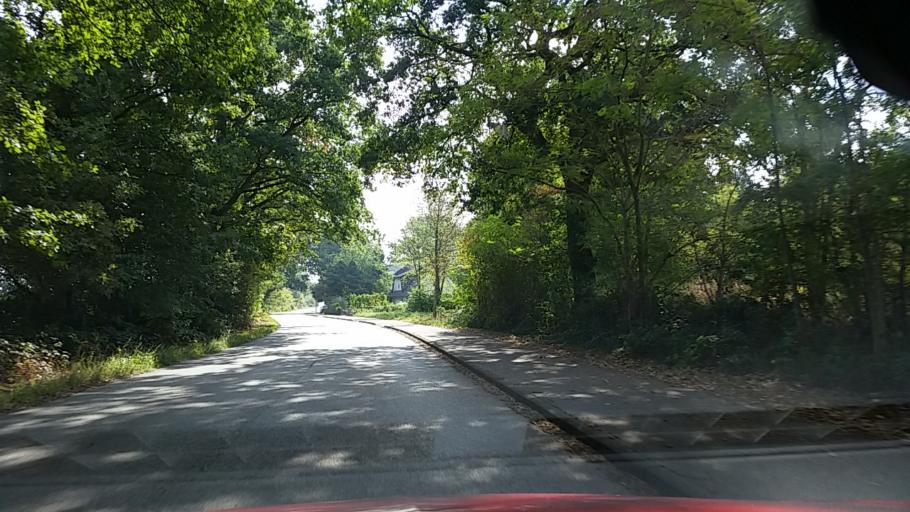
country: DE
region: Schleswig-Holstein
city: Appen
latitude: 53.6320
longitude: 9.7695
